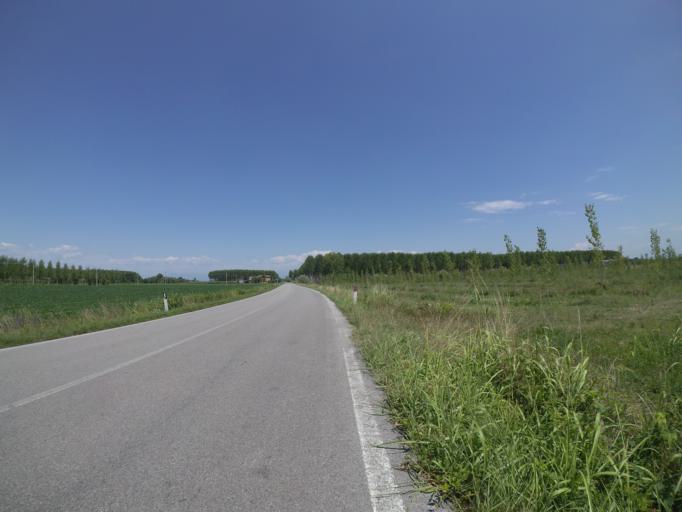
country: IT
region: Friuli Venezia Giulia
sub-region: Provincia di Udine
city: Talmassons
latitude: 45.8906
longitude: 13.1272
